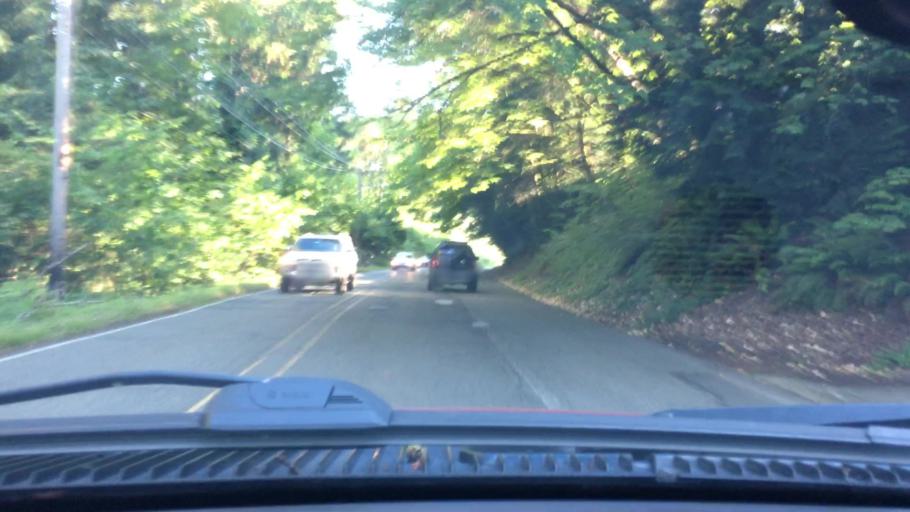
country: US
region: Washington
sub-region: King County
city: Sammamish
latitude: 47.6236
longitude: -122.0907
